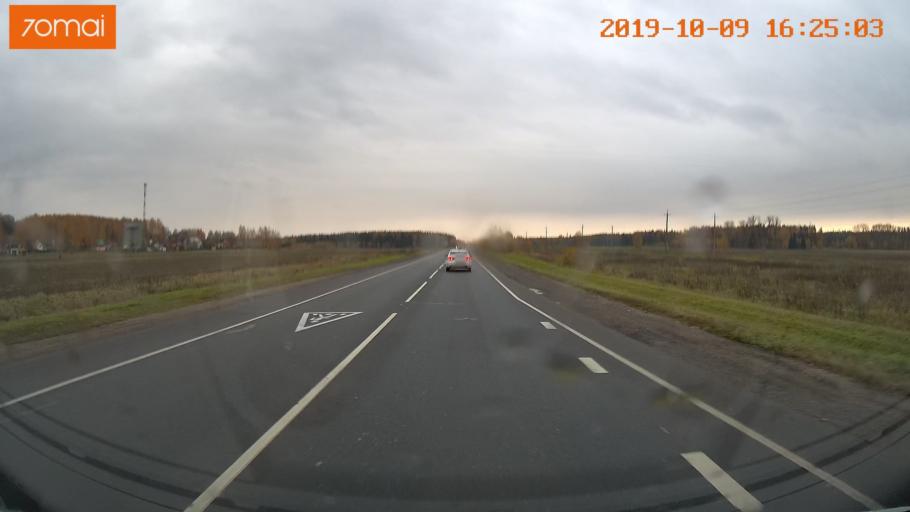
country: RU
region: Kostroma
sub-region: Kostromskoy Rayon
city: Kostroma
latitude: 57.6461
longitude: 40.9163
